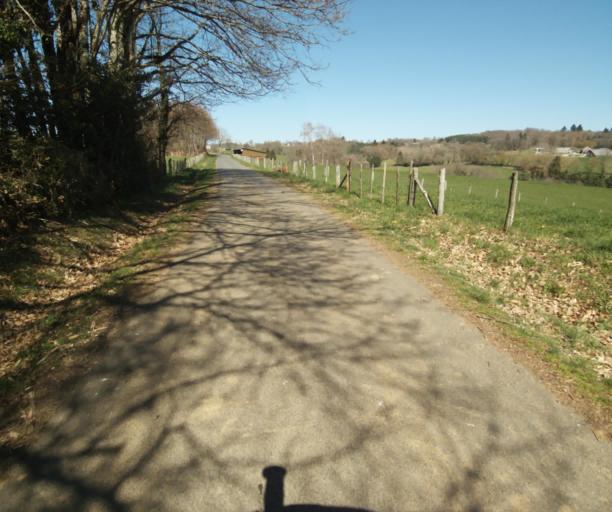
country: FR
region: Limousin
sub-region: Departement de la Correze
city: Saint-Clement
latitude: 45.3287
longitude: 1.7111
